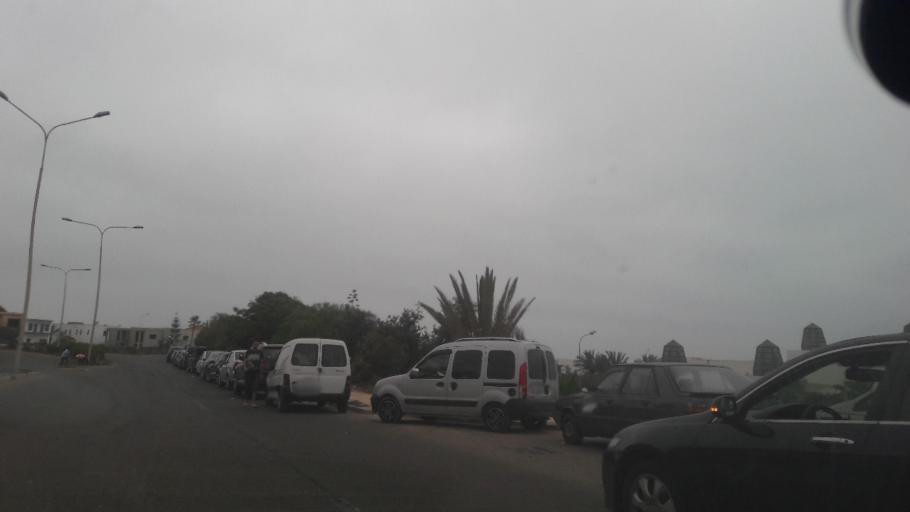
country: MA
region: Souss-Massa-Draa
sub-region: Agadir-Ida-ou-Tnan
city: Agadir
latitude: 30.3941
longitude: -9.5954
